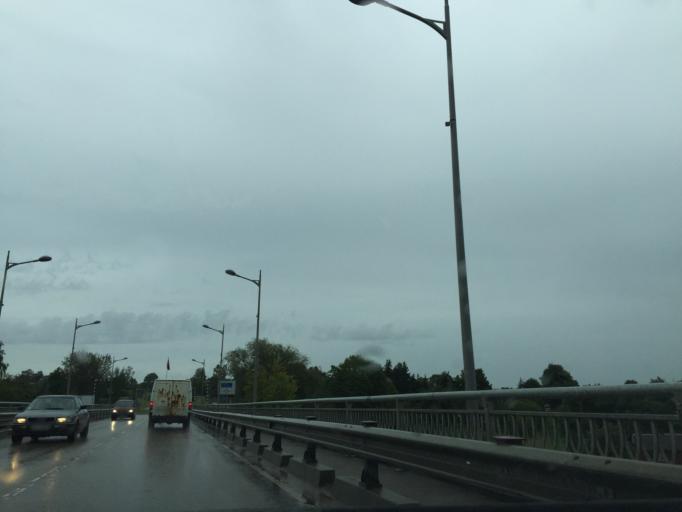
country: LV
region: Jekabpils Rajons
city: Jekabpils
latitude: 56.5002
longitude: 25.8785
